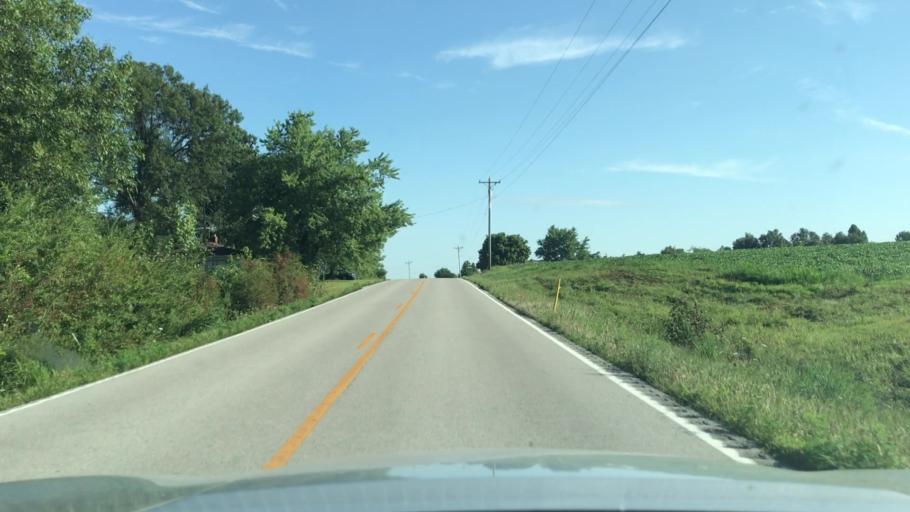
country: US
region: Kentucky
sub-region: Muhlenberg County
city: Greenville
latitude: 37.0082
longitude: -87.1309
